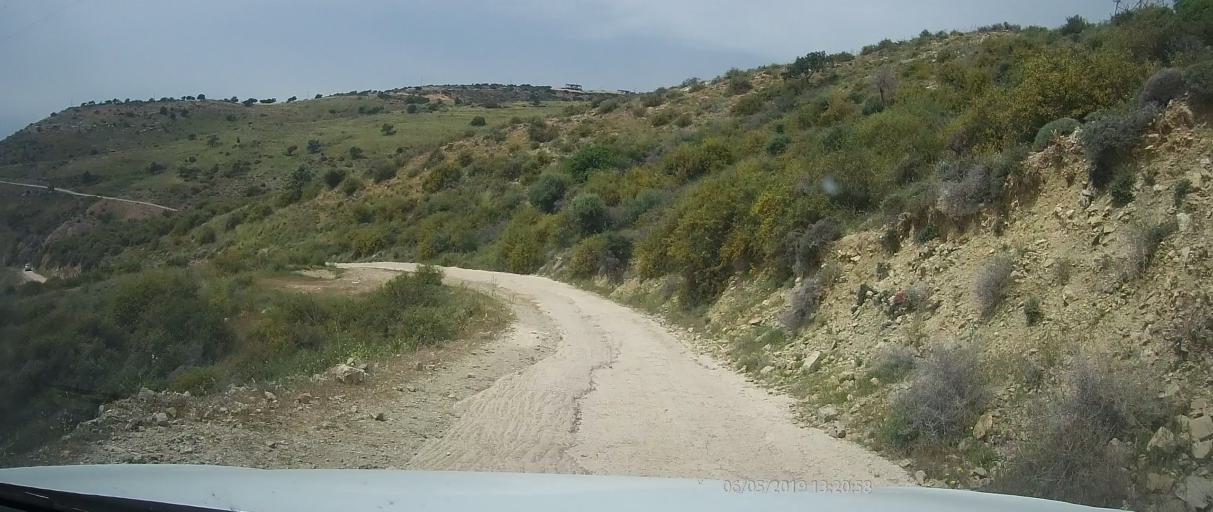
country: CY
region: Pafos
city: Tala
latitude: 34.8641
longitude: 32.4147
